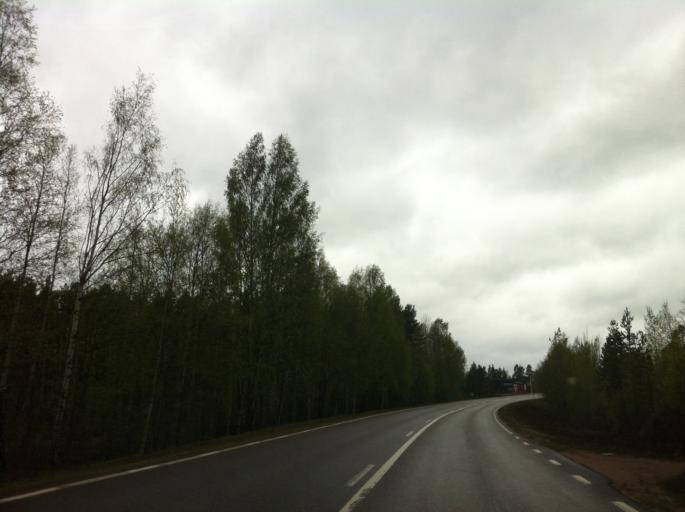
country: SE
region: Jaemtland
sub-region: Harjedalens Kommun
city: Sveg
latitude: 62.1246
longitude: 14.0815
